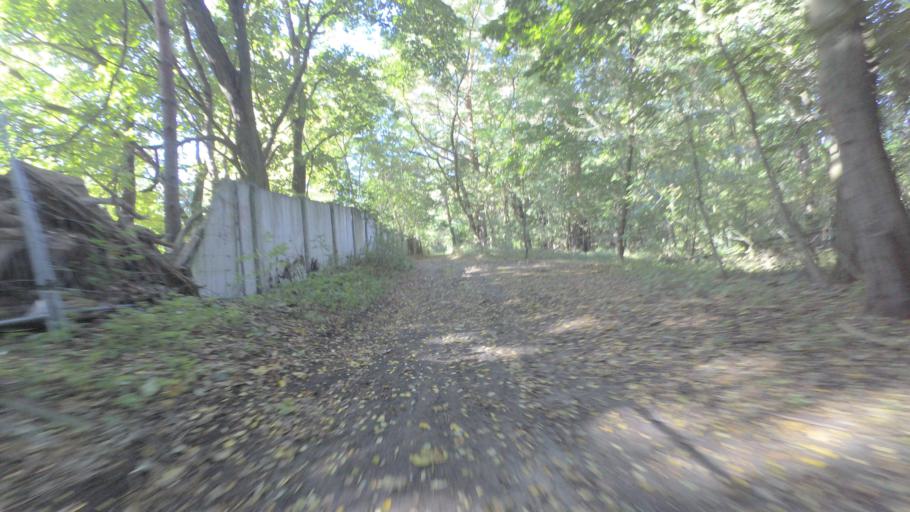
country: DE
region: Brandenburg
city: Sperenberg
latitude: 52.1498
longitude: 13.3464
